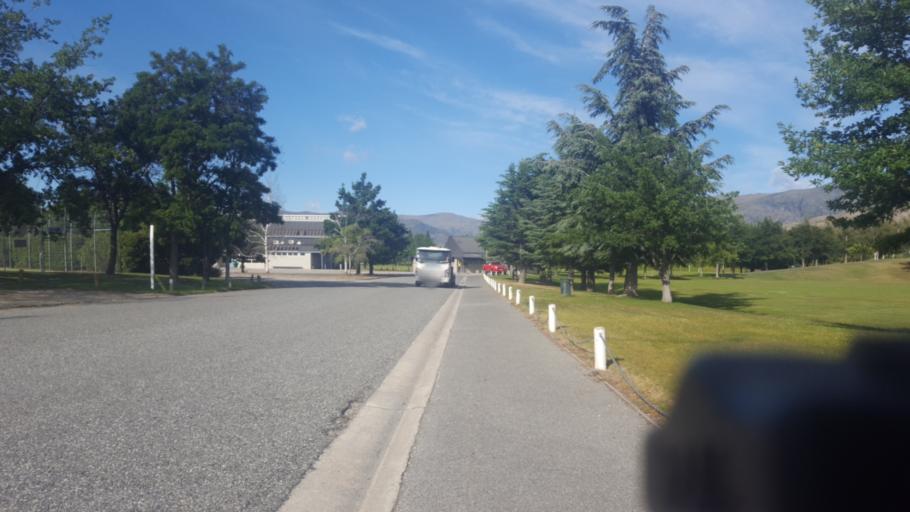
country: NZ
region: Otago
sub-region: Queenstown-Lakes District
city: Wanaka
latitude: -45.0417
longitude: 169.1959
